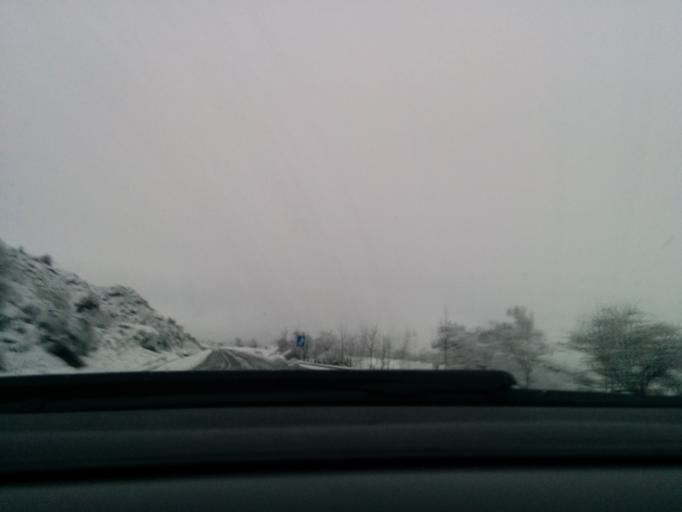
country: ES
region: Navarre
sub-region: Provincia de Navarra
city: Elorz
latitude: 42.7892
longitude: -1.5474
